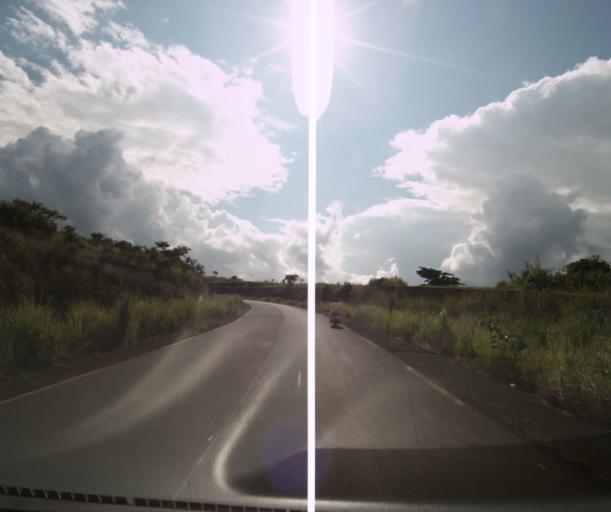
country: CM
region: West
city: Foumban
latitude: 5.7056
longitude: 10.8344
